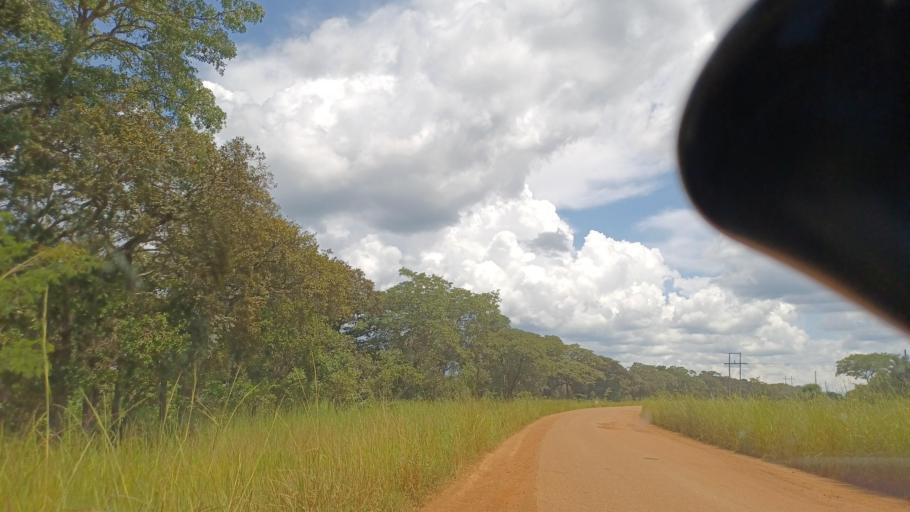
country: ZM
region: North-Western
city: Solwezi
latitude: -12.6958
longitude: 26.0399
